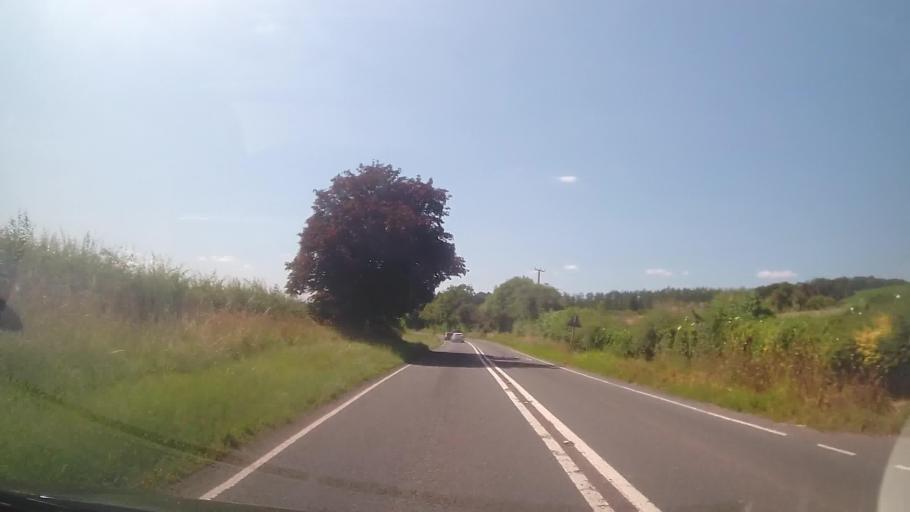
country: GB
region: England
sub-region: Herefordshire
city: Withington
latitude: 52.0789
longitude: -2.6124
